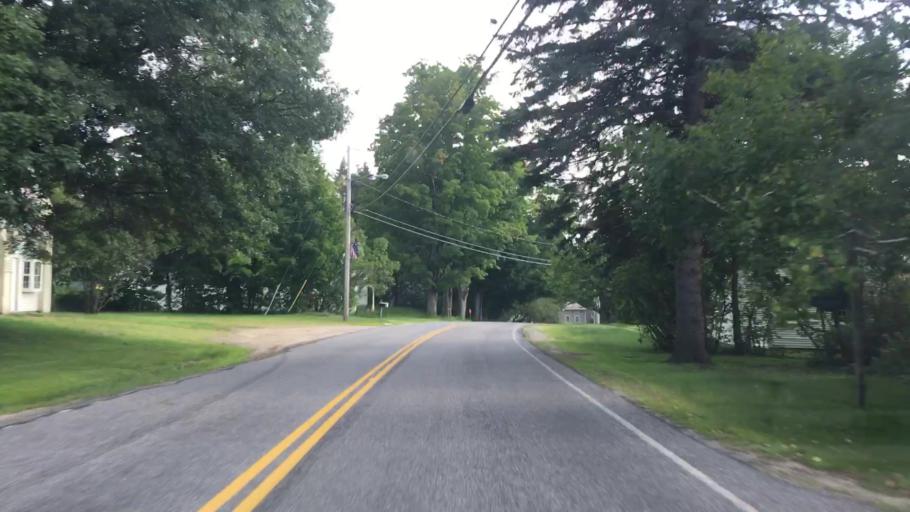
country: US
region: New Hampshire
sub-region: Belknap County
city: Sanbornton
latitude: 43.4905
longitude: -71.5831
